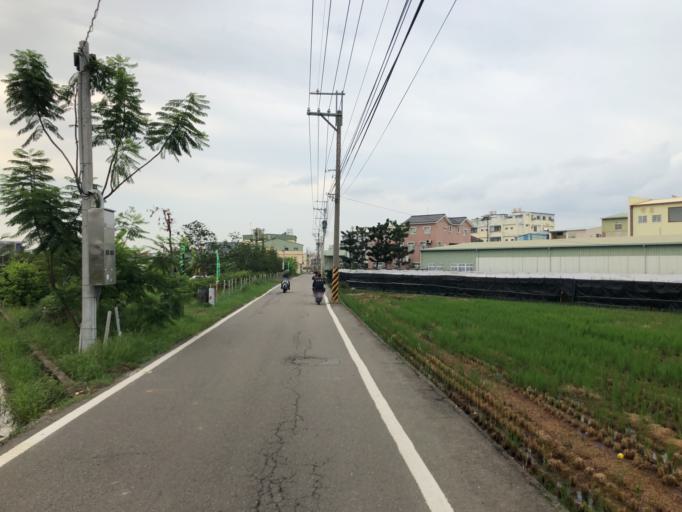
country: TW
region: Taiwan
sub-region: Taichung City
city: Taichung
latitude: 24.0574
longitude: 120.6847
